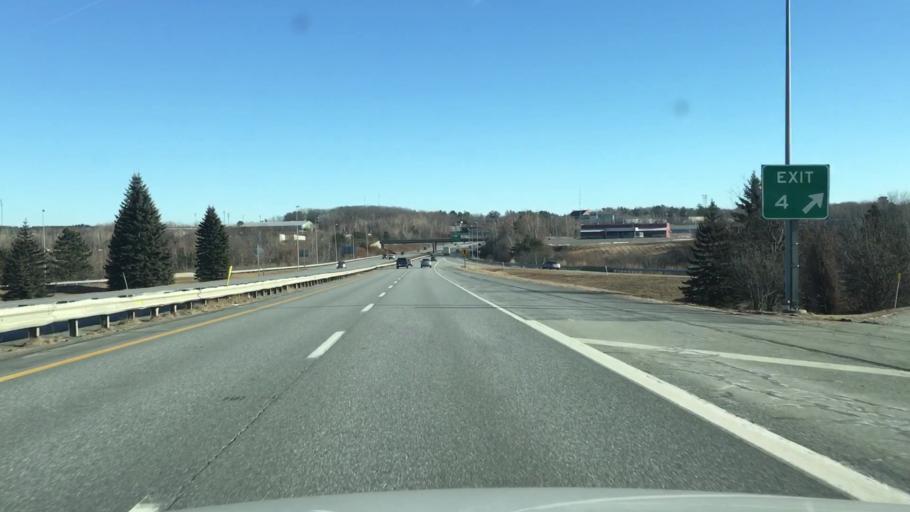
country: US
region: Maine
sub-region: Penobscot County
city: Brewer
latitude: 44.7836
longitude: -68.7714
